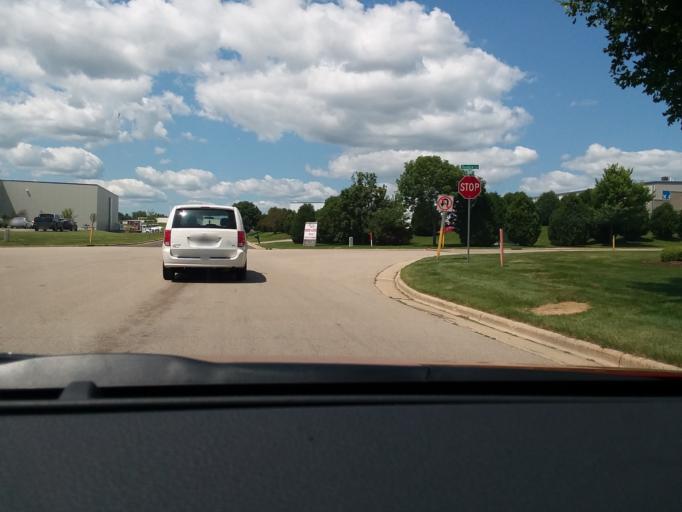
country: US
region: Wisconsin
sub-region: Dane County
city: Windsor
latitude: 43.1998
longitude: -89.3339
